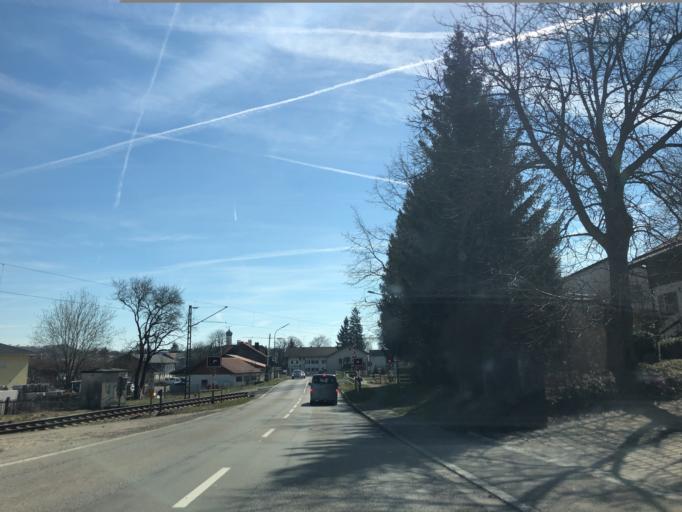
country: DE
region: Bavaria
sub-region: Upper Bavaria
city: Grafing bei Munchen
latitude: 48.0510
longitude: 11.9637
